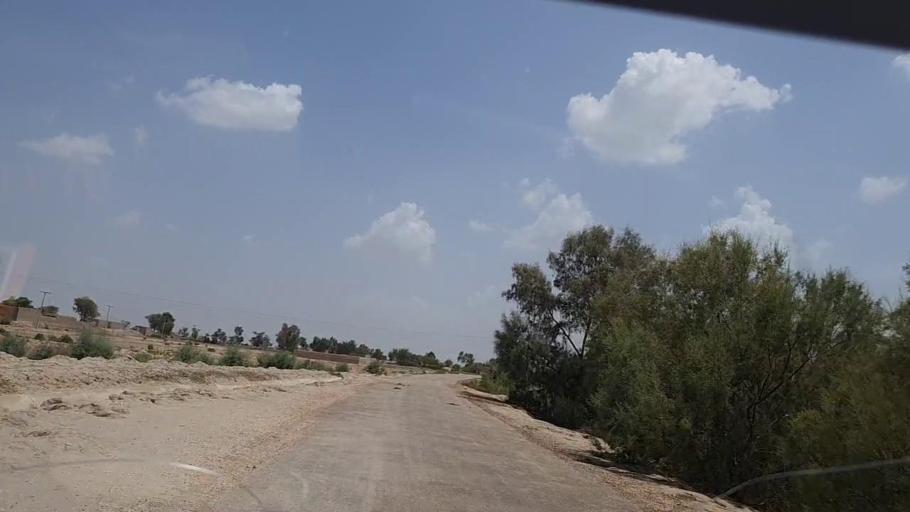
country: PK
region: Sindh
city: Bhan
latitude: 26.5171
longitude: 67.6388
